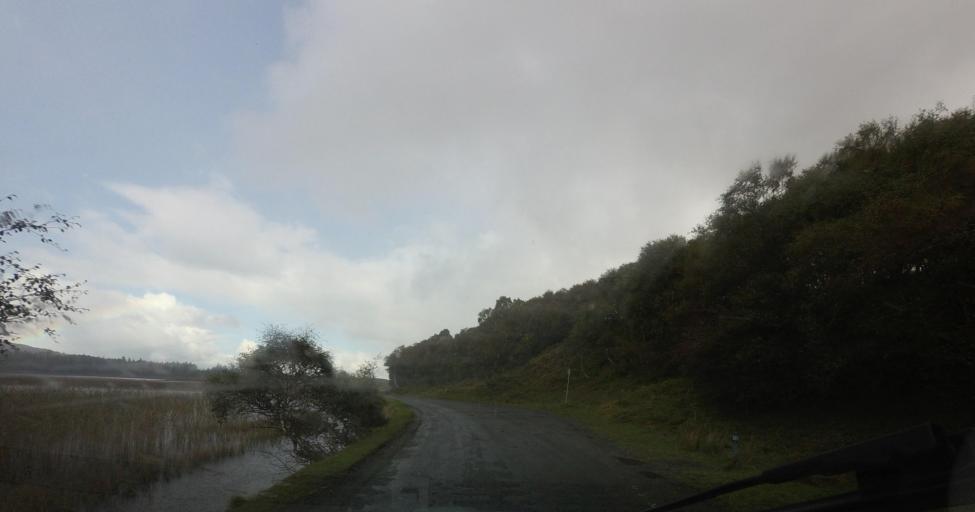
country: GB
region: Scotland
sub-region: Highland
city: Portree
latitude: 57.2114
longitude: -5.9546
